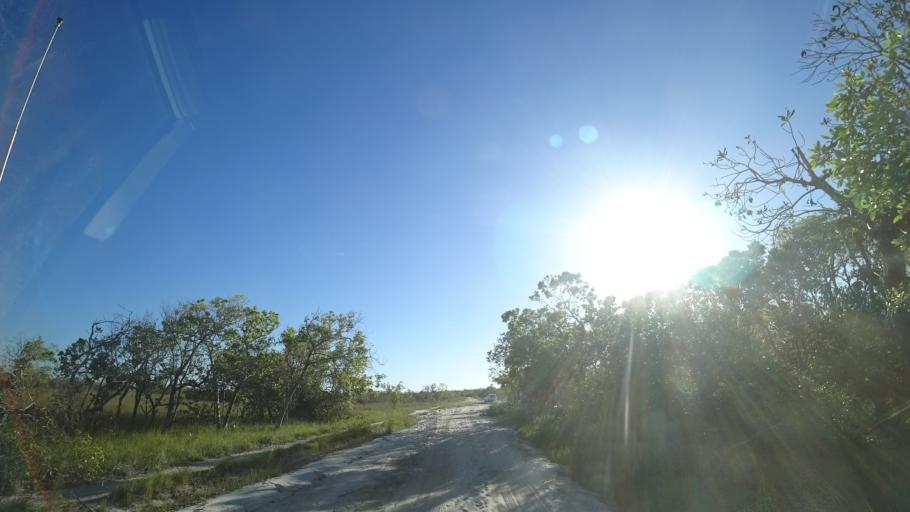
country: MZ
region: Sofala
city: Beira
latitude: -19.5764
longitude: 35.1972
